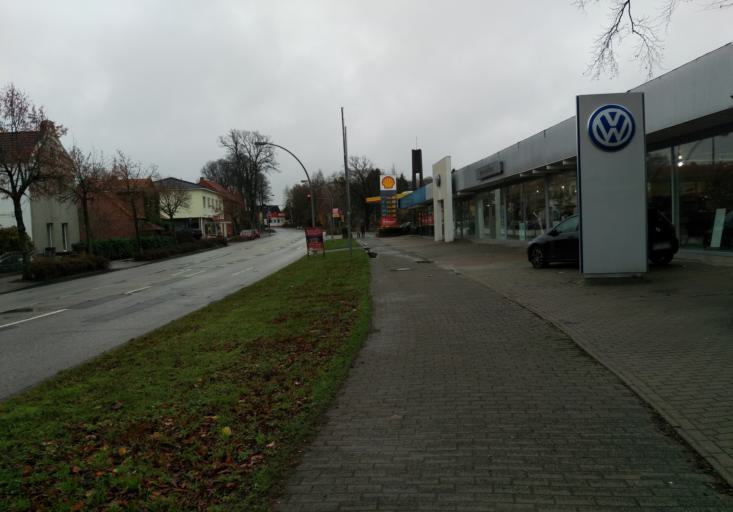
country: DE
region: Schleswig-Holstein
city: Oldenburg in Holstein
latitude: 54.2869
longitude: 10.8804
